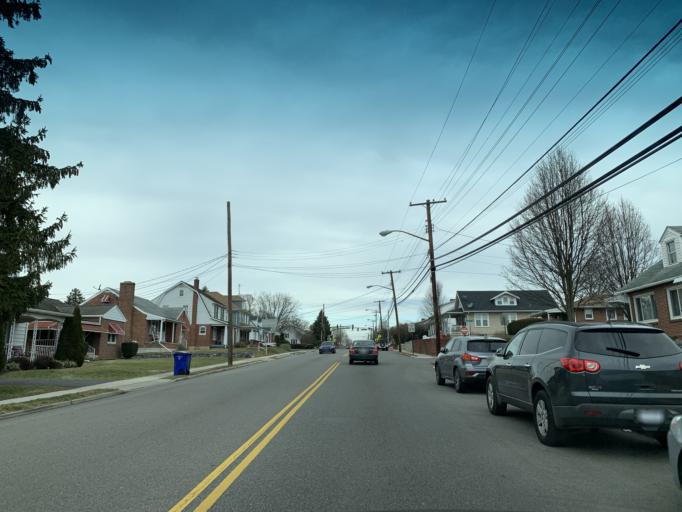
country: US
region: Maryland
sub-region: Washington County
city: Hagerstown
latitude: 39.6559
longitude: -77.7332
